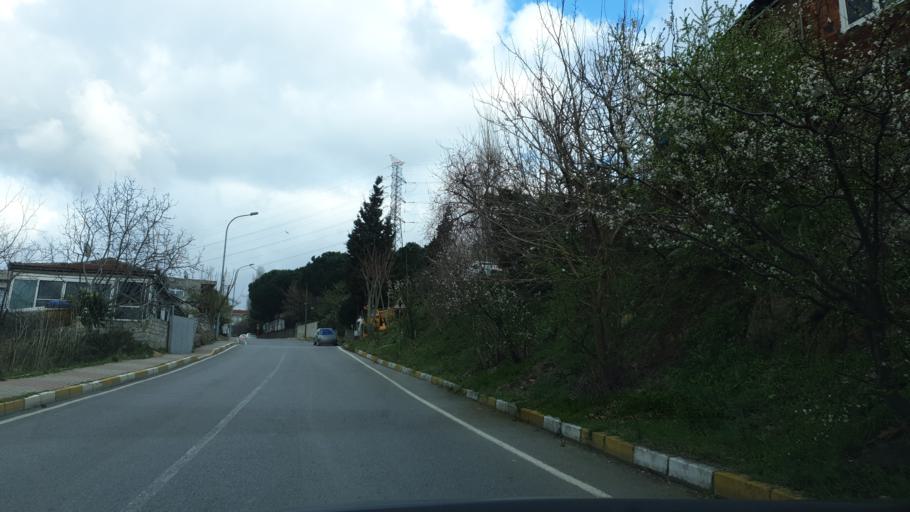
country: TR
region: Istanbul
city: Pendik
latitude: 40.8987
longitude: 29.2395
